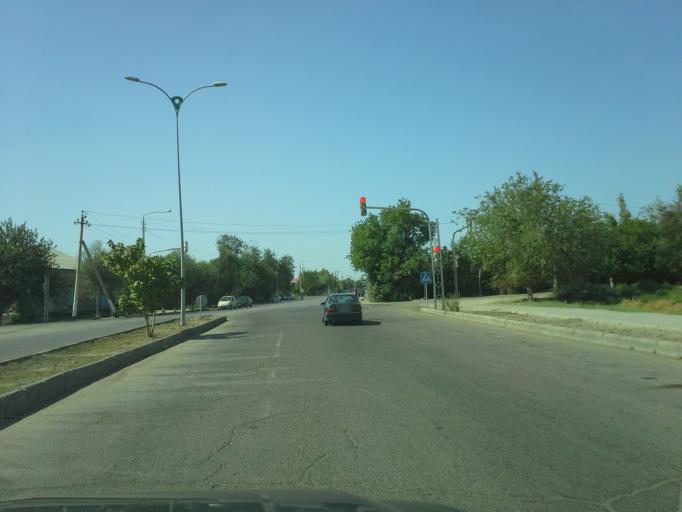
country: TM
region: Dasoguz
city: Dasoguz
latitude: 41.8115
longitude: 59.9920
